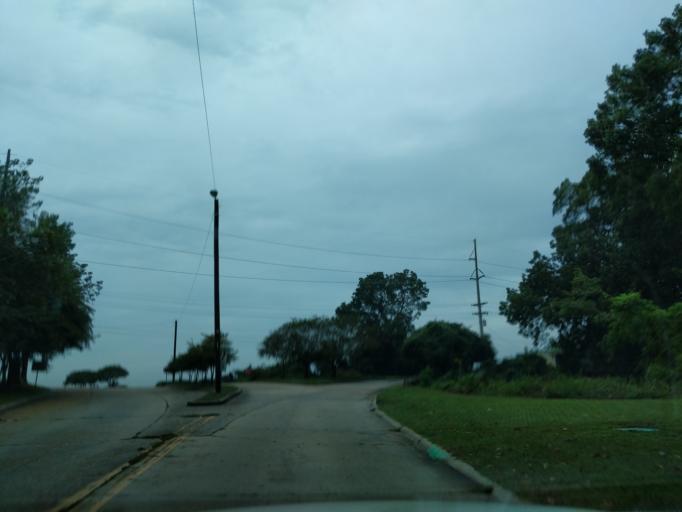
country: US
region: Mississippi
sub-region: Warren County
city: Vicksburg
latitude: 32.3184
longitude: -90.8960
